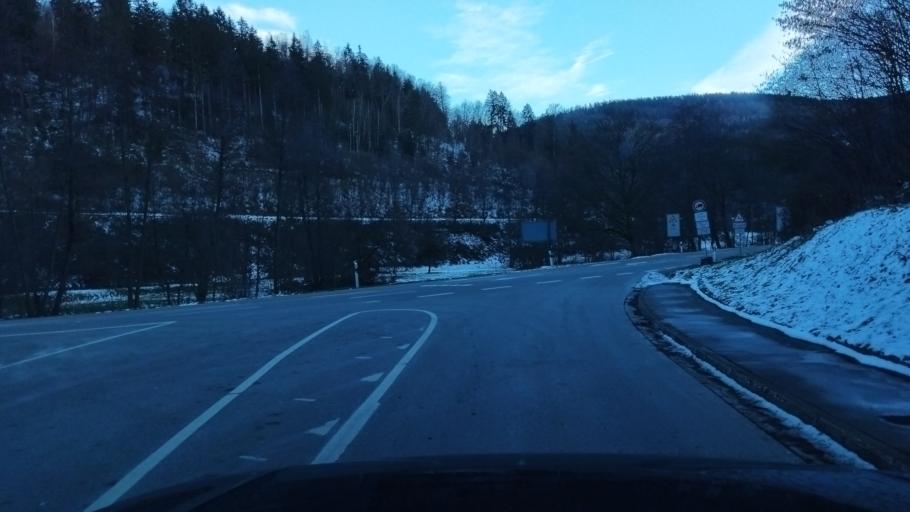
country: DE
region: Baden-Wuerttemberg
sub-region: Karlsruhe Region
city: Eberbach
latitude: 49.4945
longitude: 9.0450
